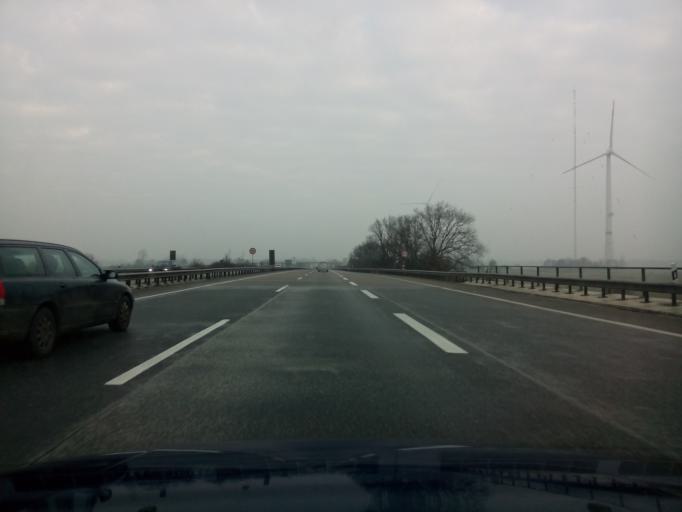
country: DE
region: Lower Saxony
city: Schiffdorf
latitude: 53.5511
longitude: 8.6198
